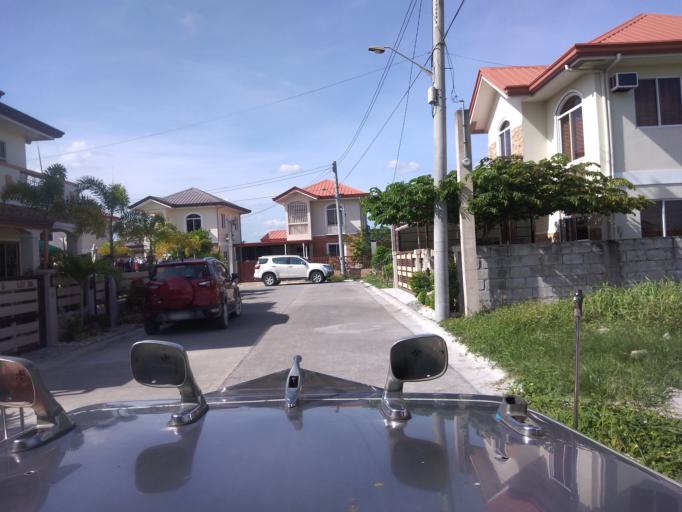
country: PH
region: Central Luzon
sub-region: Province of Pampanga
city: Magliman
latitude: 15.0247
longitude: 120.6600
